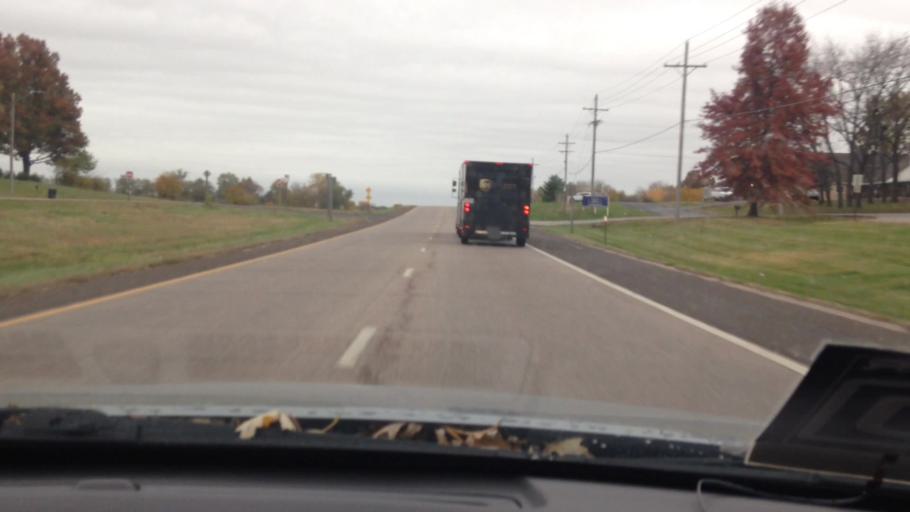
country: US
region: Kansas
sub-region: Leavenworth County
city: Lansing
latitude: 39.2064
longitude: -94.9004
